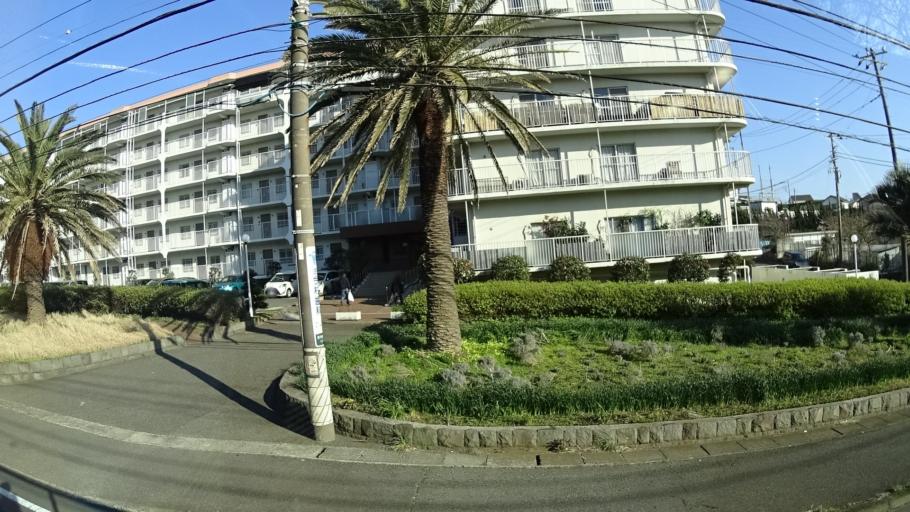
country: JP
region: Kanagawa
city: Miura
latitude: 35.1600
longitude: 139.6395
